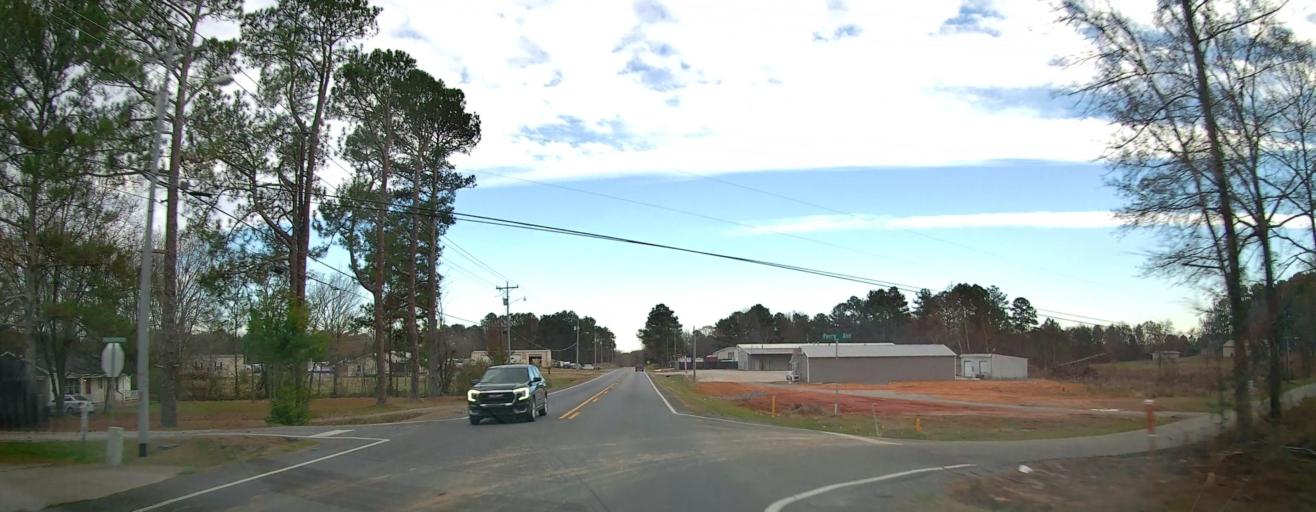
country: US
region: Alabama
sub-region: Morgan County
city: Priceville
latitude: 34.4961
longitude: -86.8472
